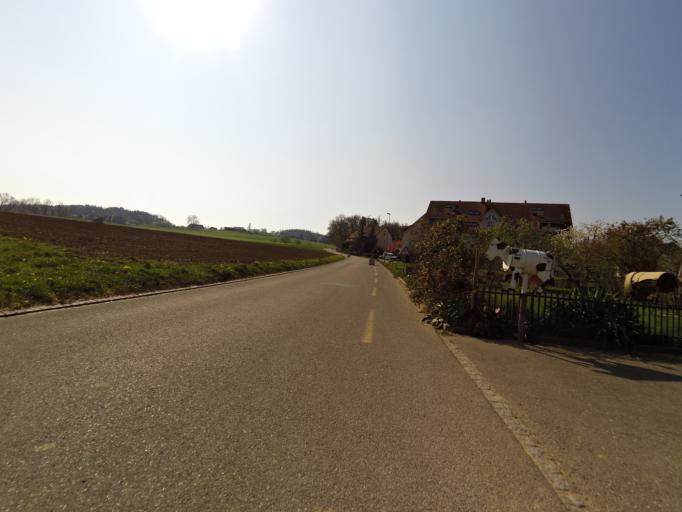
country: CH
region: Thurgau
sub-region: Frauenfeld District
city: Gachnang
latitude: 47.5493
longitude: 8.8620
